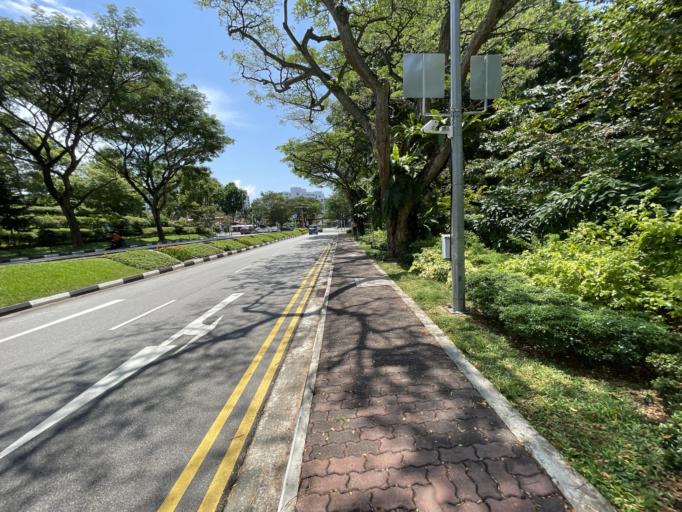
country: SG
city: Singapore
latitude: 1.3014
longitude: 103.7713
